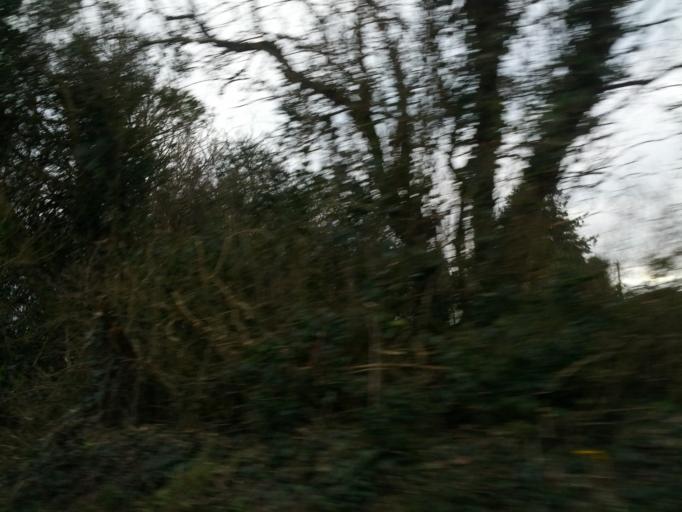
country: IE
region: Connaught
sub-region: County Galway
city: Oranmore
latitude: 53.1726
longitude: -8.8909
